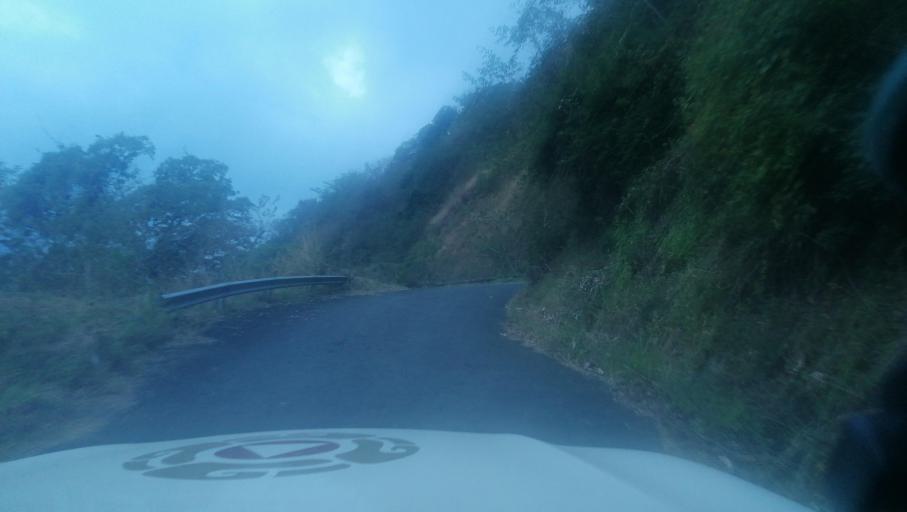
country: MX
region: Chiapas
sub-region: Cacahoatan
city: Benito Juarez
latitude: 15.1400
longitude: -92.1976
